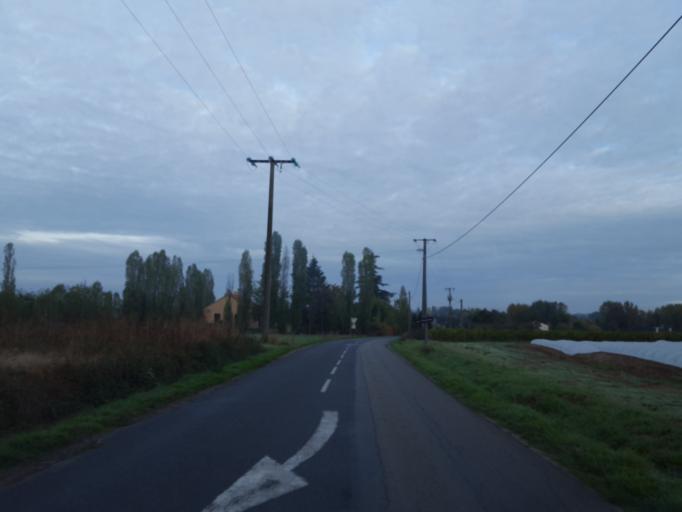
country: FR
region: Pays de la Loire
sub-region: Departement de la Loire-Atlantique
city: Saint-Julien-de-Concelles
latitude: 47.2476
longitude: -1.4014
